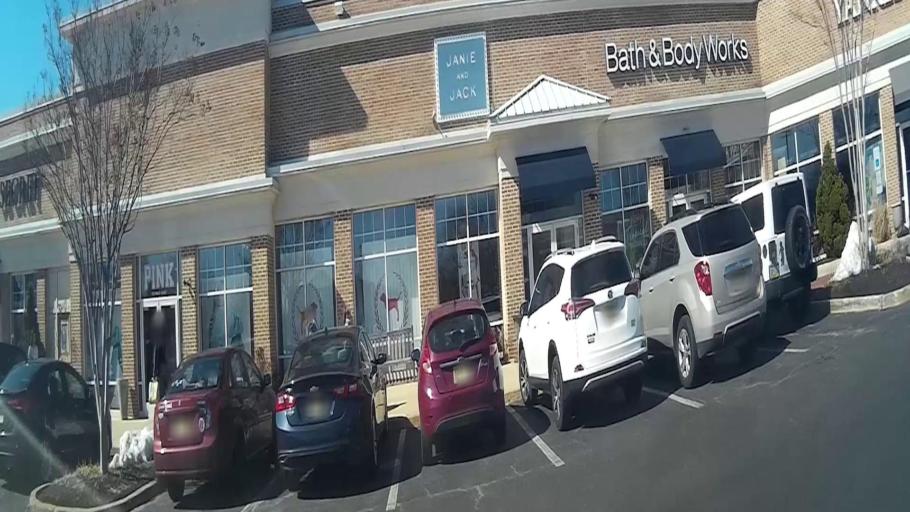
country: US
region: New Jersey
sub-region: Burlington County
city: Marlton
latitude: 39.8904
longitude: -74.9243
